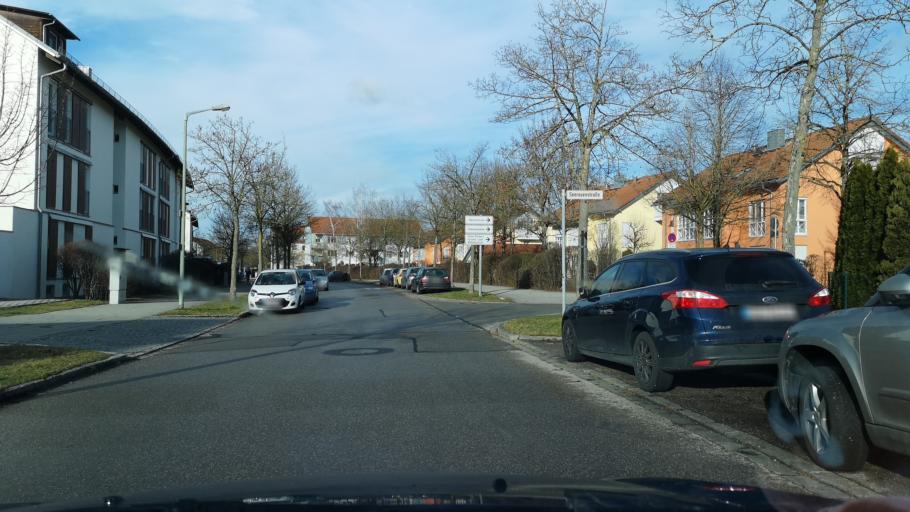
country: DE
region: Bavaria
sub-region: Upper Bavaria
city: Poing
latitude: 48.1747
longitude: 11.8070
